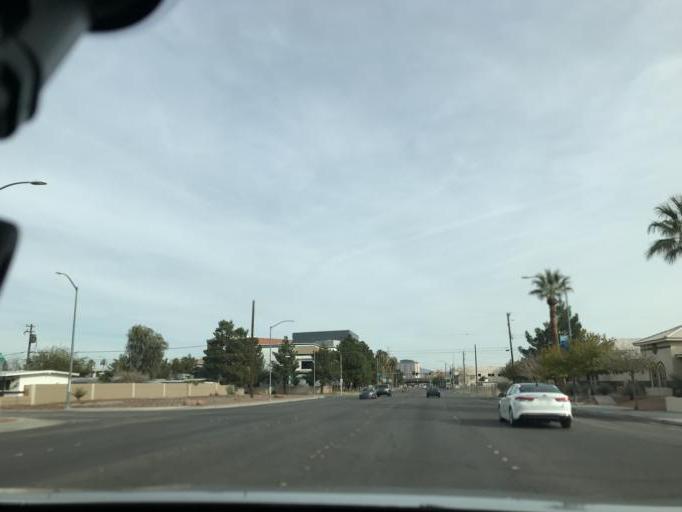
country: US
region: Nevada
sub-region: Clark County
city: Las Vegas
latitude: 36.1663
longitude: -115.1679
